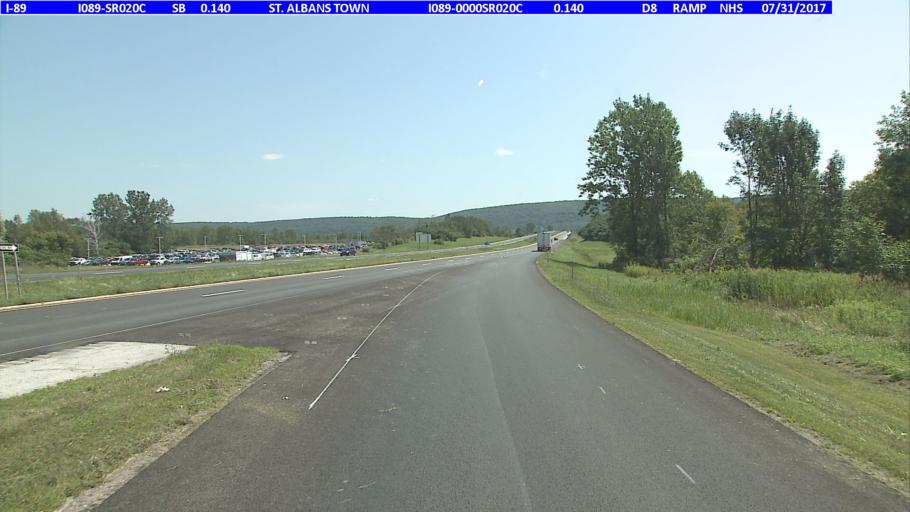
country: US
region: Vermont
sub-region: Franklin County
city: Saint Albans
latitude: 44.8425
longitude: -73.0776
